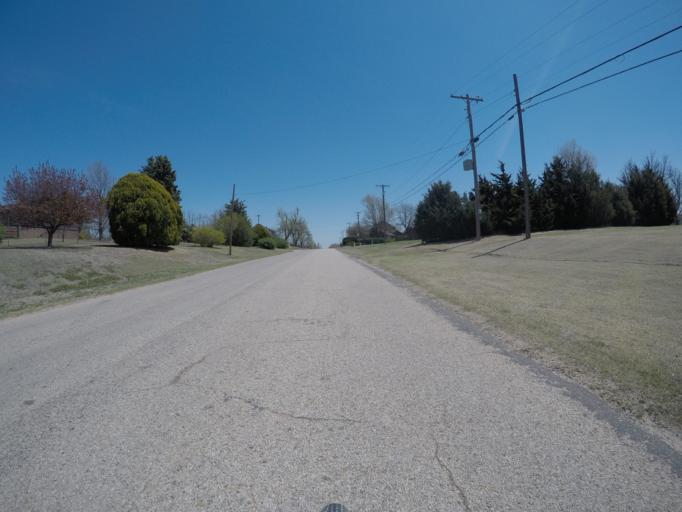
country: US
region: Kansas
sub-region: Pratt County
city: Pratt
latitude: 37.6420
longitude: -98.7563
